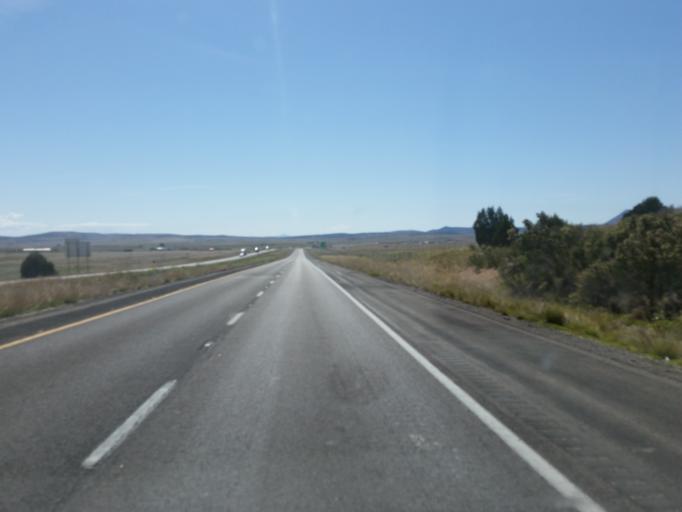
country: US
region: Arizona
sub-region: Mohave County
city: Peach Springs
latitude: 35.3179
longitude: -112.8816
